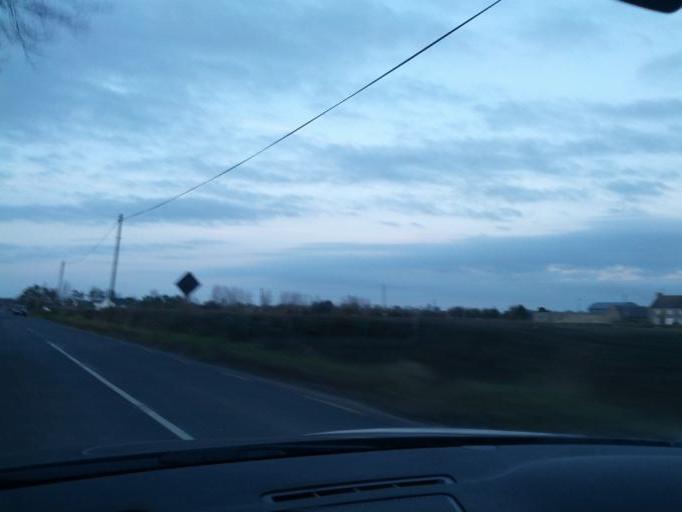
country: IE
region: Connaught
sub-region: County Galway
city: Portumna
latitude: 53.0481
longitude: -8.1073
